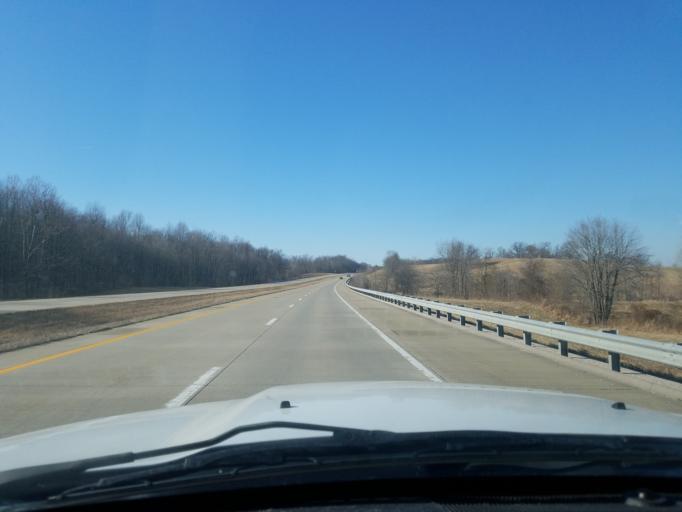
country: US
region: Indiana
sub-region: Warrick County
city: Newburgh
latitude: 37.7553
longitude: -87.4067
